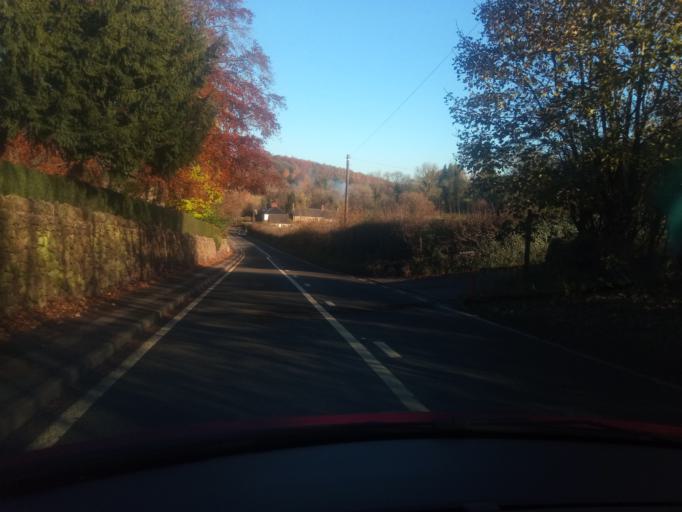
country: GB
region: England
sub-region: Derbyshire
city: Belper
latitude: 53.0247
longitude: -1.5111
